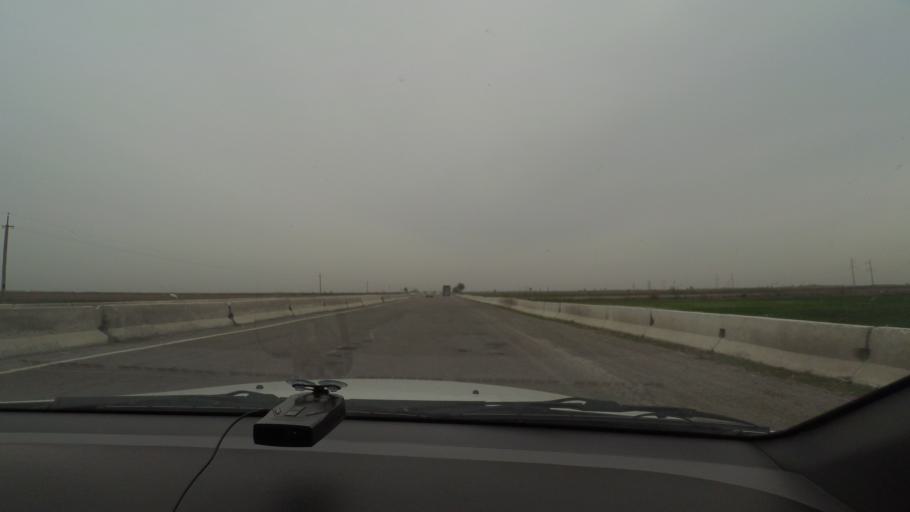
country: KZ
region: Ongtustik Qazaqstan
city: Myrzakent
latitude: 40.5215
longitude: 68.4616
